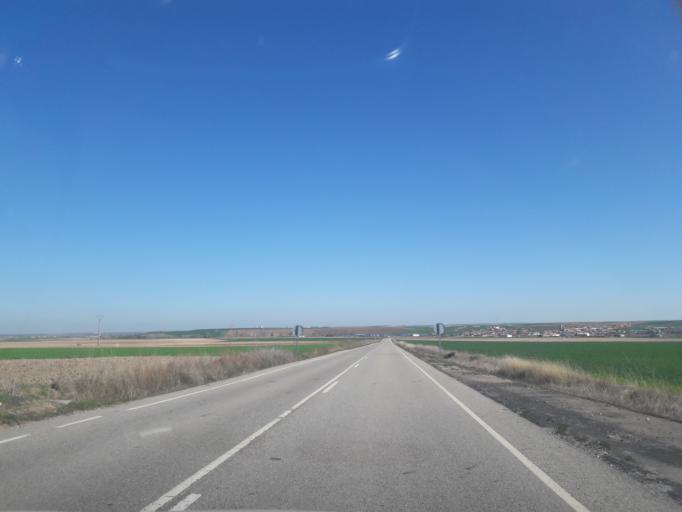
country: ES
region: Castille and Leon
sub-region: Provincia de Salamanca
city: Mancera de Abajo
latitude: 40.8252
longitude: -5.2086
